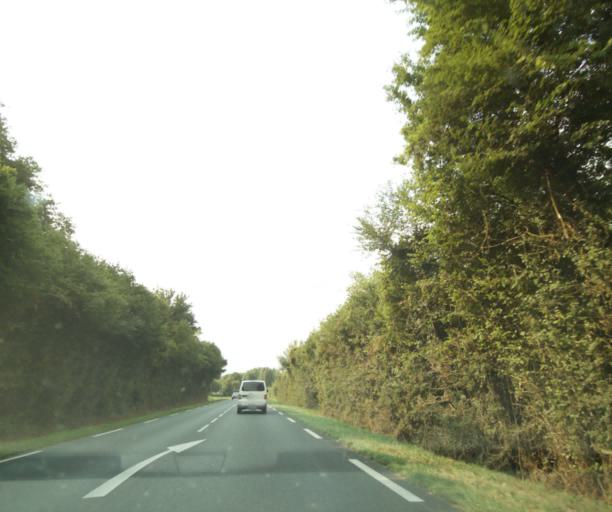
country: FR
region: Centre
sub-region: Departement de l'Indre
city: Chatillon-sur-Indre
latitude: 46.9675
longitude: 1.2003
